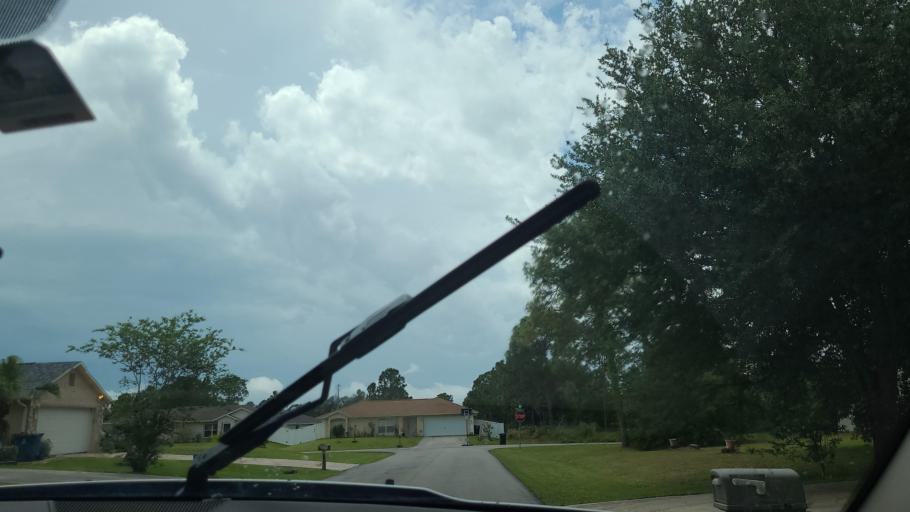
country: US
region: Florida
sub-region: Brevard County
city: Grant-Valkaria
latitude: 27.9455
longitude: -80.6376
